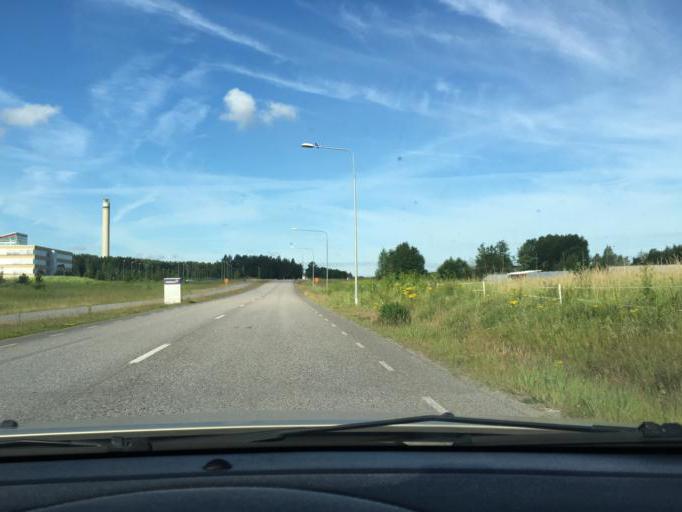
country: SE
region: Stockholm
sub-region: Sodertalje Kommun
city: Pershagen
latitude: 59.1825
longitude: 17.6785
